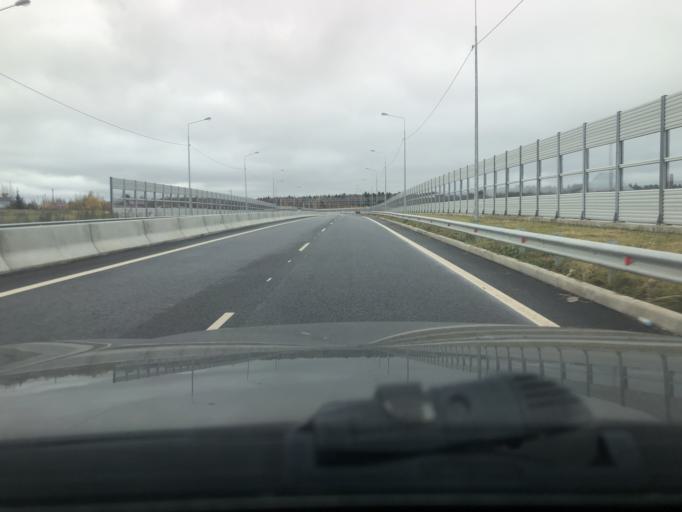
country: RU
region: Moskovskaya
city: Semkhoz
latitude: 56.3268
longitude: 38.0774
